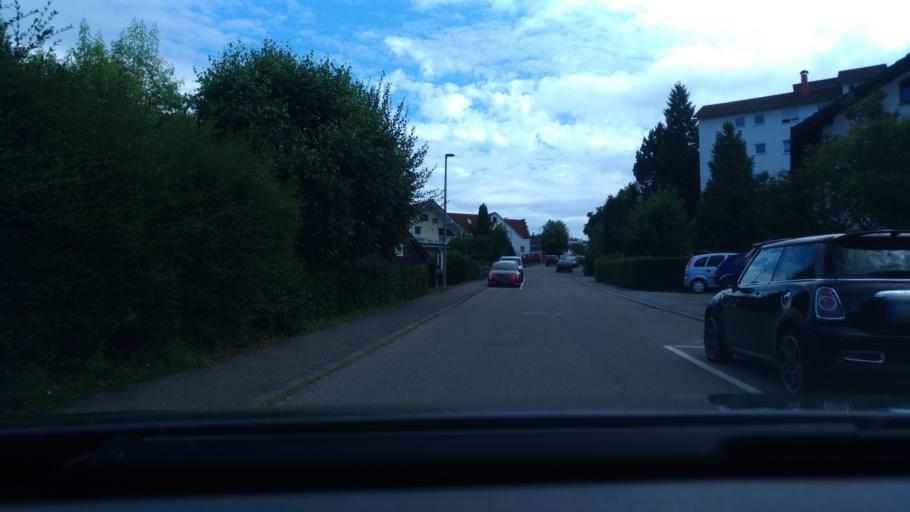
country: DE
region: Baden-Wuerttemberg
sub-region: Freiburg Region
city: Stockach
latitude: 47.8621
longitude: 9.0100
